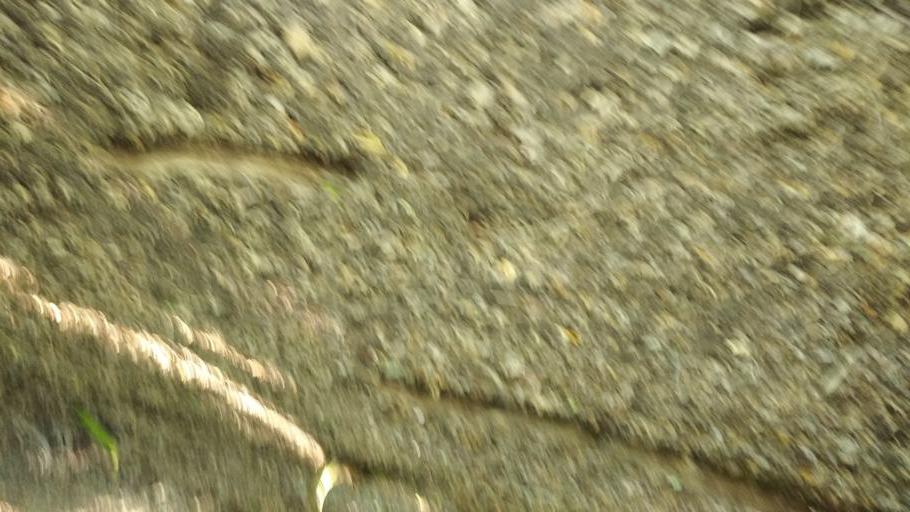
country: HU
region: Pest
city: Nagymaros
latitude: 47.7866
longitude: 18.9246
